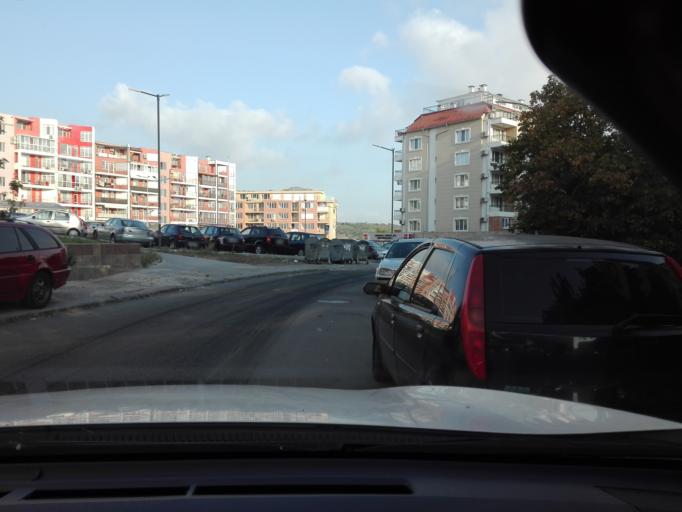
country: BG
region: Burgas
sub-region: Obshtina Burgas
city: Burgas
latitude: 42.4626
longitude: 27.4145
